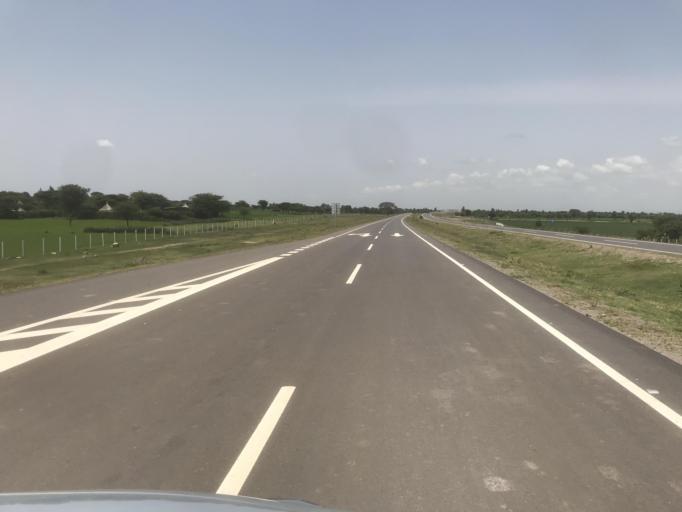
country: ET
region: Oromiya
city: Ziway
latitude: 8.2655
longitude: 38.9041
